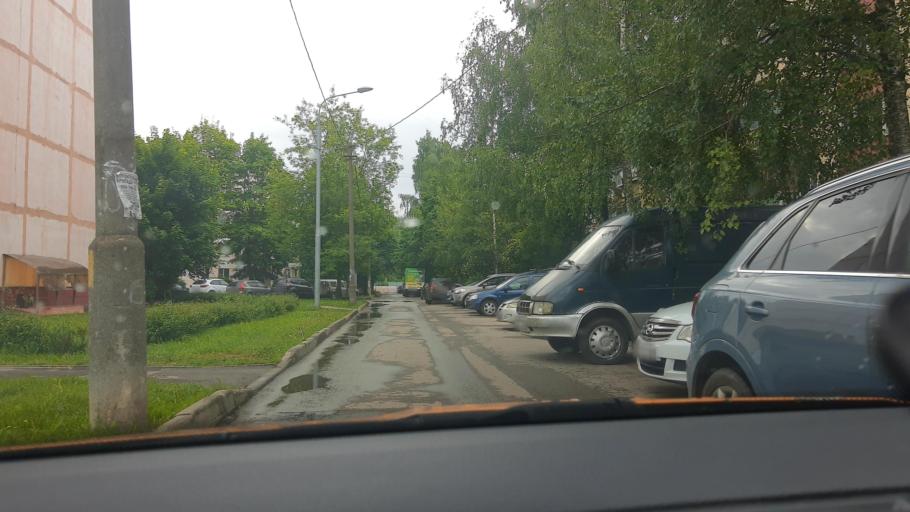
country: RU
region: Moskovskaya
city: Kievskij
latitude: 55.4288
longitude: 36.8673
